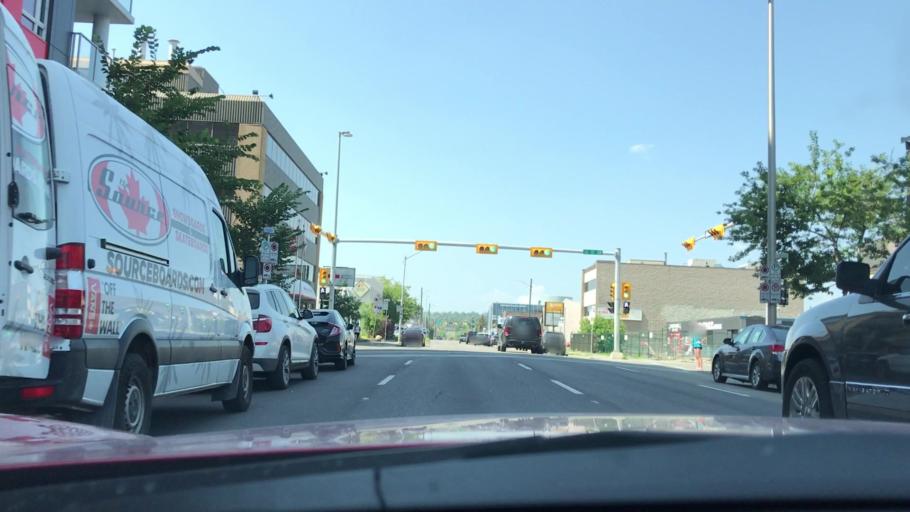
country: CA
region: Alberta
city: Calgary
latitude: 51.0432
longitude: -114.0908
